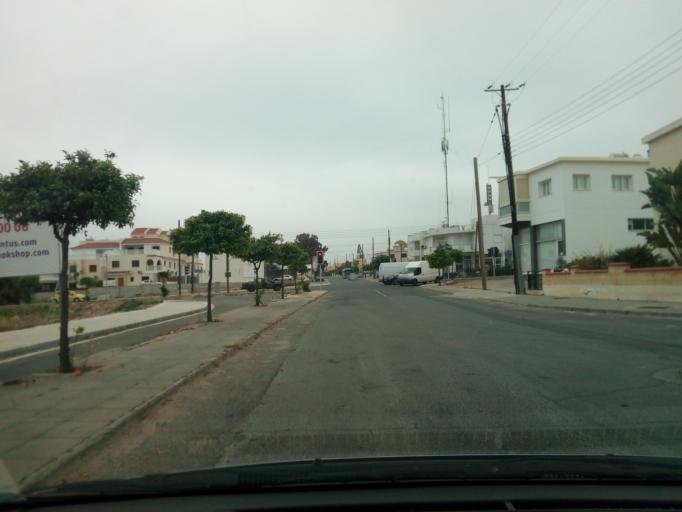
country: CY
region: Ammochostos
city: Paralimni
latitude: 35.0530
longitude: 33.9838
